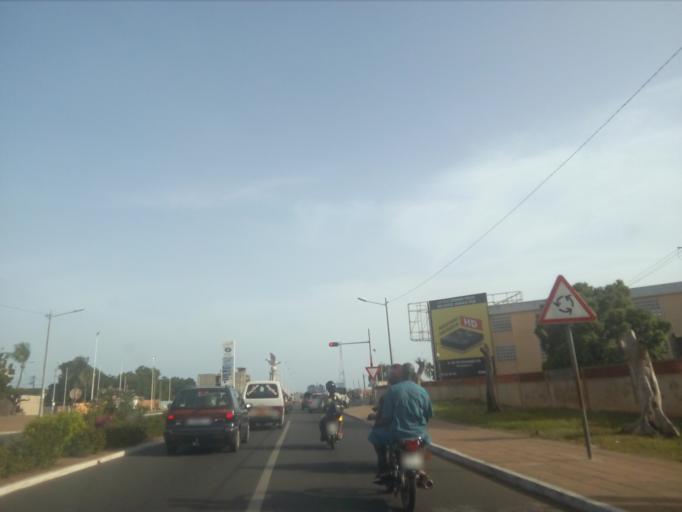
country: TG
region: Maritime
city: Lome
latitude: 6.1513
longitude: 1.2295
